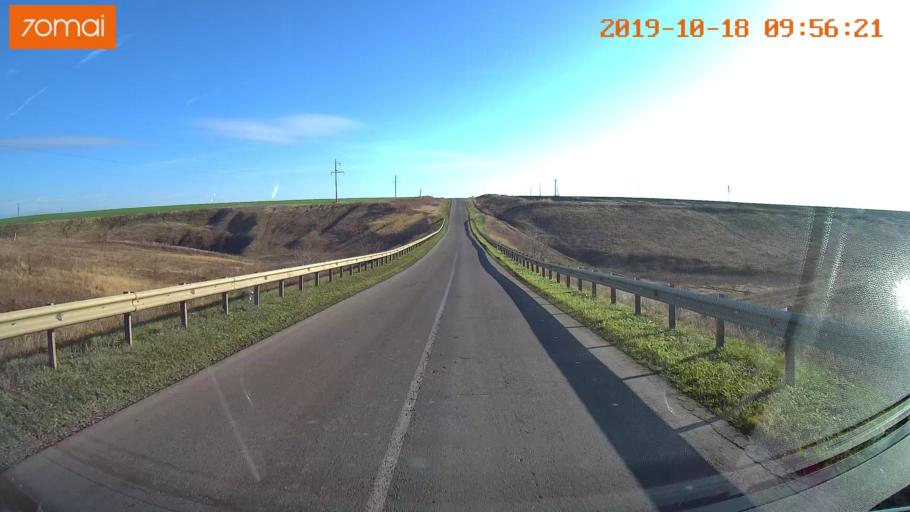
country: RU
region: Tula
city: Kurkino
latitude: 53.3738
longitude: 38.3878
